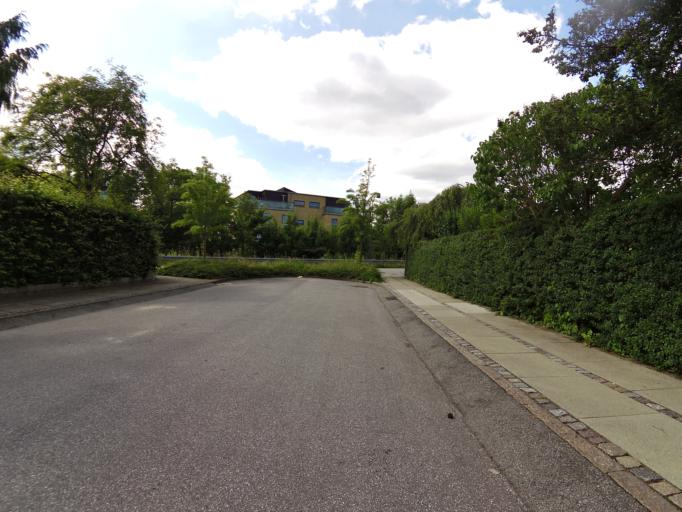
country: DK
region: Capital Region
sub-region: Frederiksberg Kommune
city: Frederiksberg
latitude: 55.7248
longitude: 12.5411
